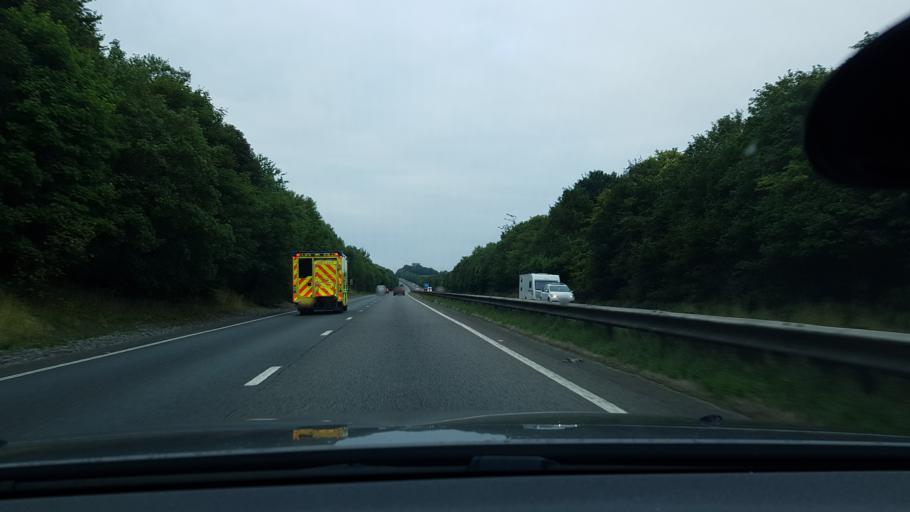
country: GB
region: England
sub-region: Hampshire
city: Kings Worthy
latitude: 51.1316
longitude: -1.3449
